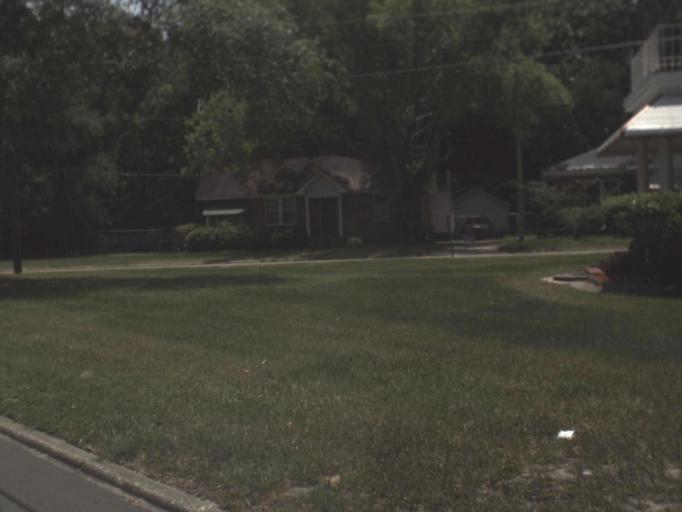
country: US
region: Florida
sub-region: Duval County
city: Jacksonville
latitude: 30.3848
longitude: -81.6557
